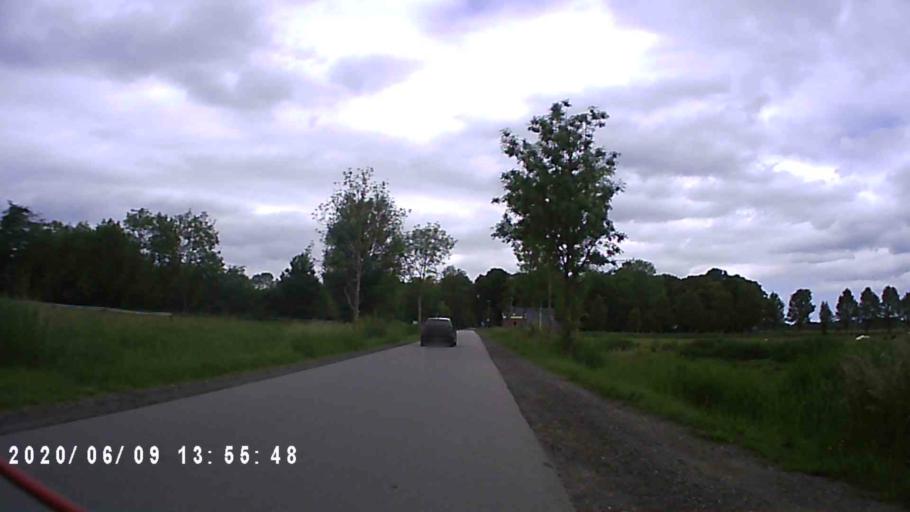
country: NL
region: Groningen
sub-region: Gemeente Groningen
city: Oosterpark
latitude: 53.2426
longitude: 6.6286
